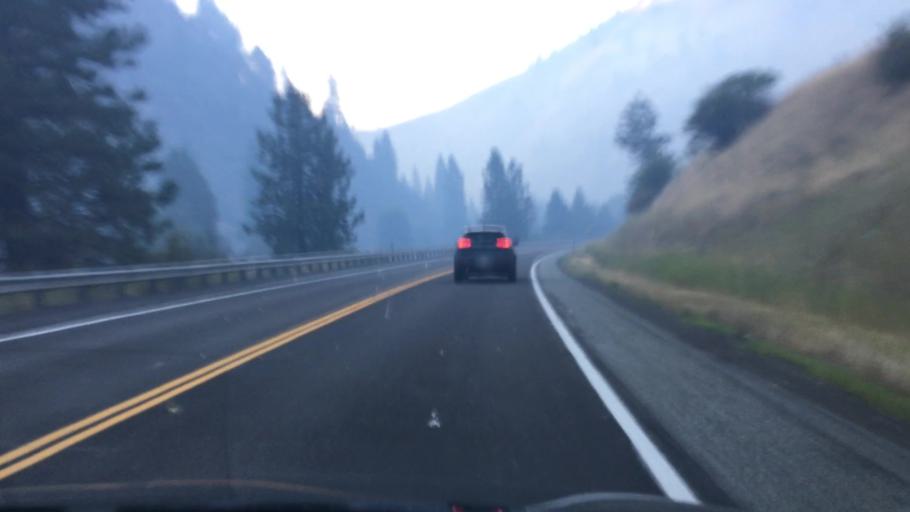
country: US
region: Idaho
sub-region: Valley County
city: McCall
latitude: 45.2737
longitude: -116.3471
